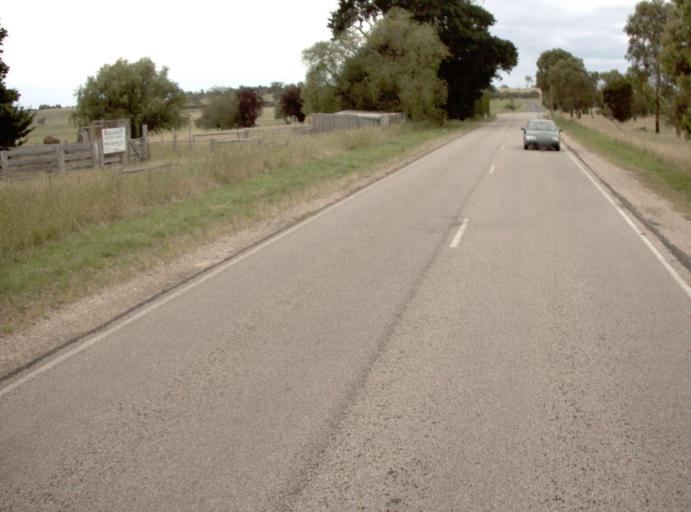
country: AU
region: Victoria
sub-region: East Gippsland
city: Bairnsdale
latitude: -37.8137
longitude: 147.4893
